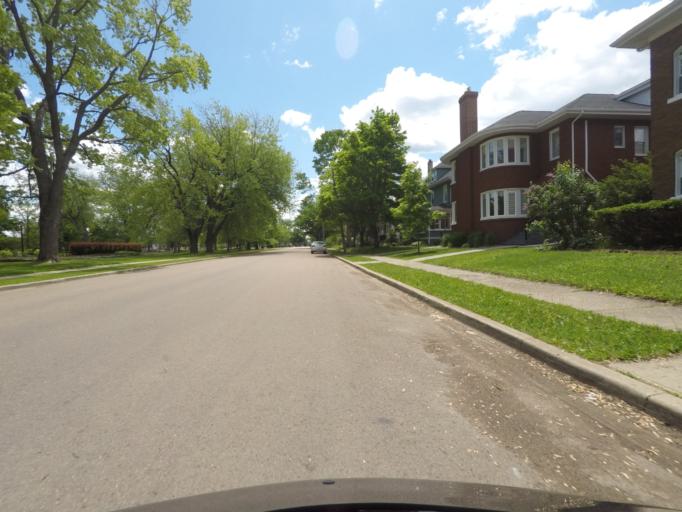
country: CA
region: New Brunswick
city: Moncton
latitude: 46.0933
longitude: -64.7909
